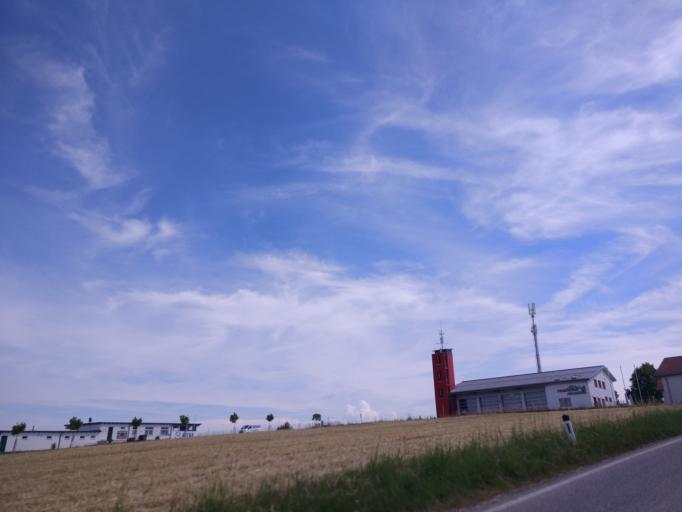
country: DE
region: Bavaria
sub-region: Upper Bavaria
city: Burghausen
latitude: 48.1486
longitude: 12.8389
